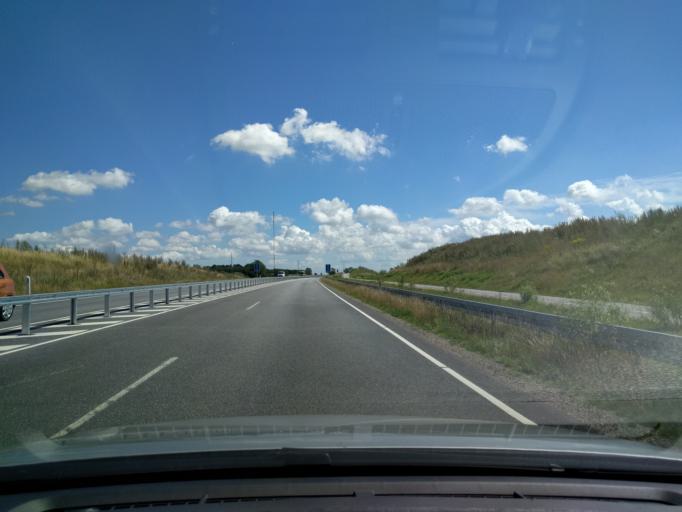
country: DK
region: Zealand
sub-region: Naestved Kommune
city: Fensmark
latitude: 55.2620
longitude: 11.7868
